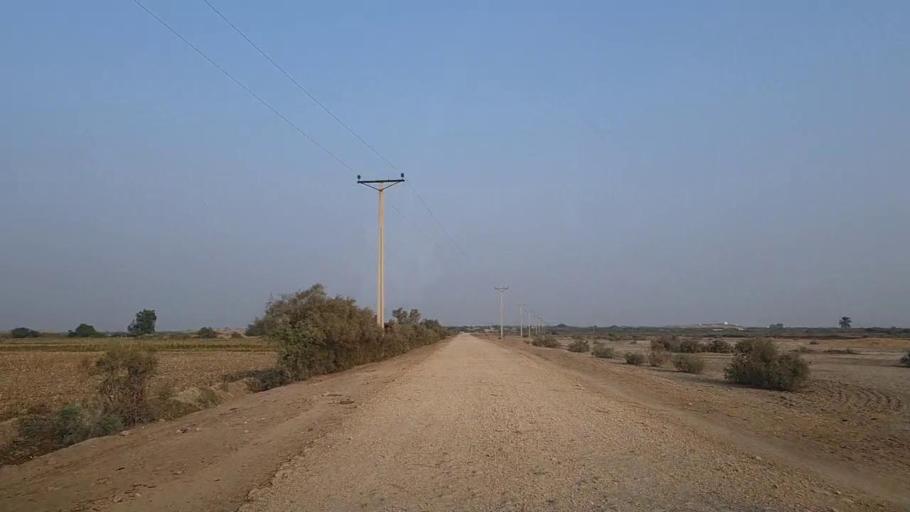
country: PK
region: Sindh
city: Thatta
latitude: 24.6903
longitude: 67.8097
